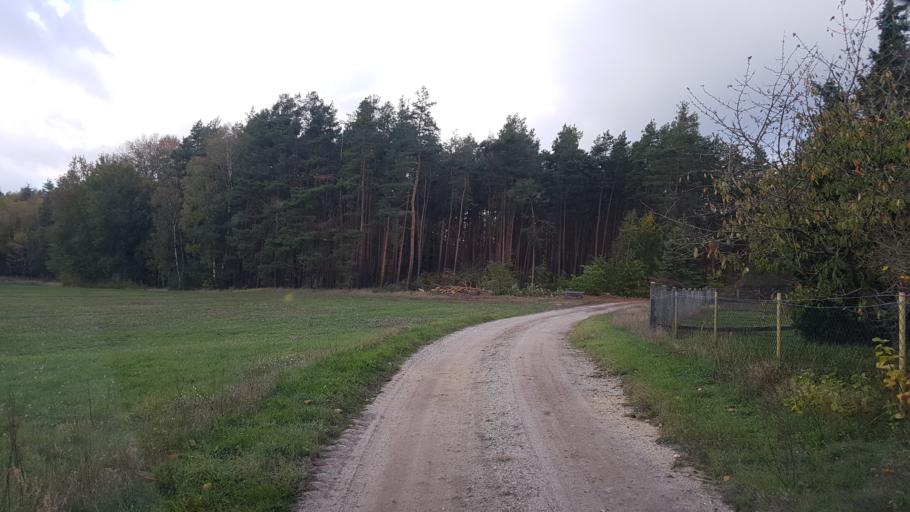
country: DE
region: Brandenburg
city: Schonborn
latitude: 51.6172
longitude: 13.5143
